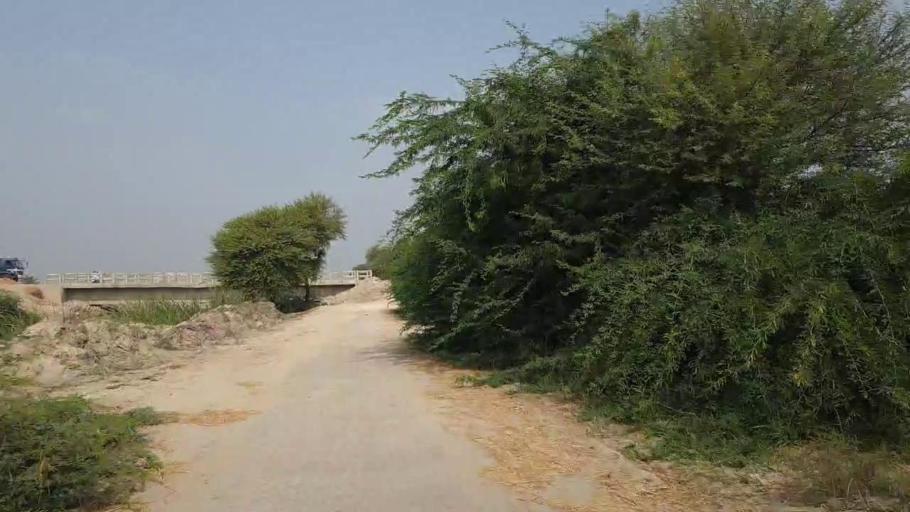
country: PK
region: Sindh
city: Kario
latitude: 24.7816
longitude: 68.5213
